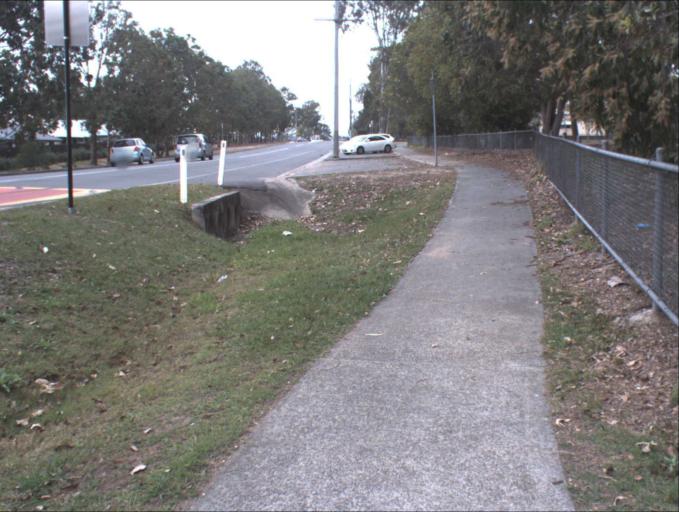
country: AU
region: Queensland
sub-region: Logan
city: Logan Reserve
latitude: -27.7137
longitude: 153.1125
